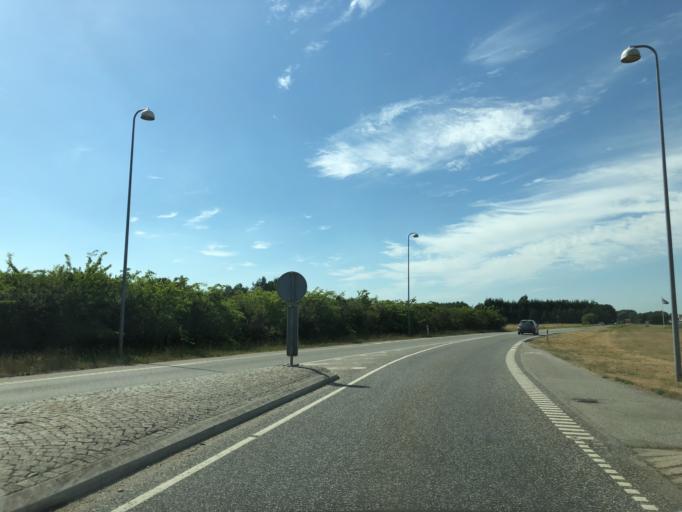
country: DK
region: Central Jutland
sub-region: Ikast-Brande Kommune
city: Brande
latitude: 55.9268
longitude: 9.1572
